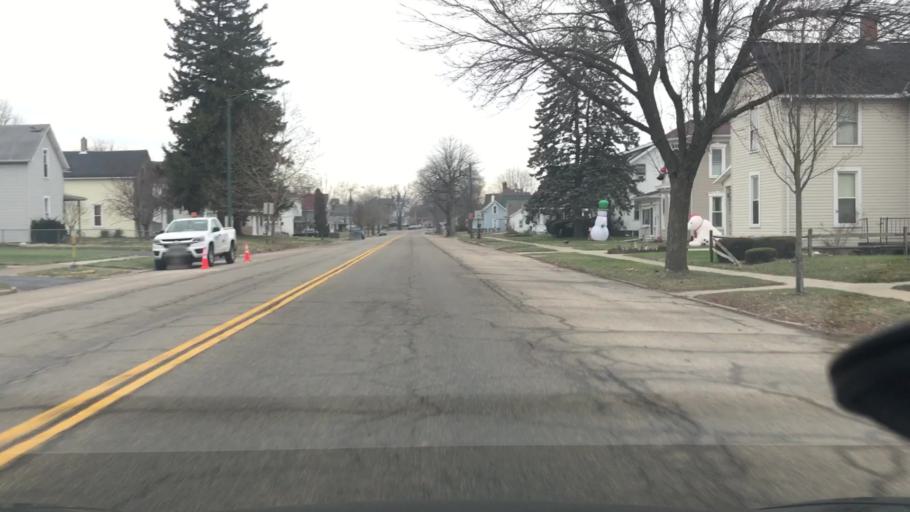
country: US
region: Ohio
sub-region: Madison County
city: London
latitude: 39.8807
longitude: -83.4410
